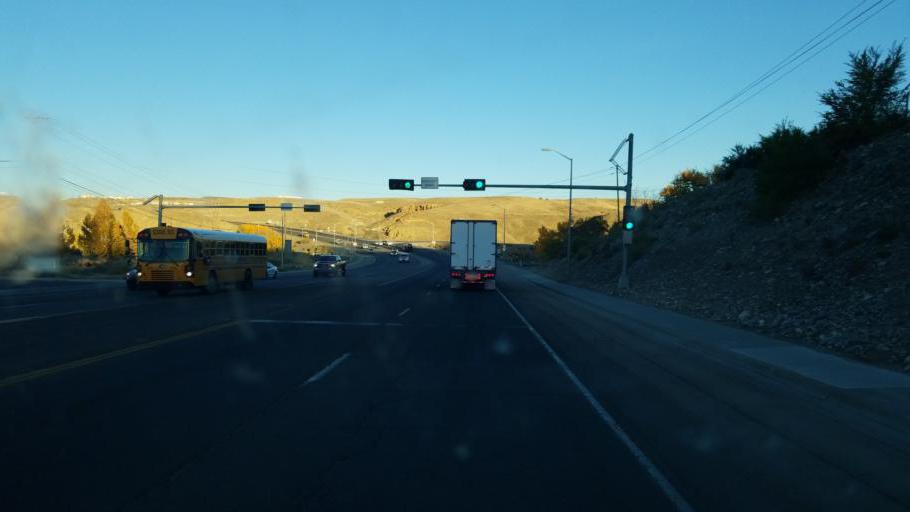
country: US
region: New Mexico
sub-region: San Juan County
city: Farmington
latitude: 36.7361
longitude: -108.2485
